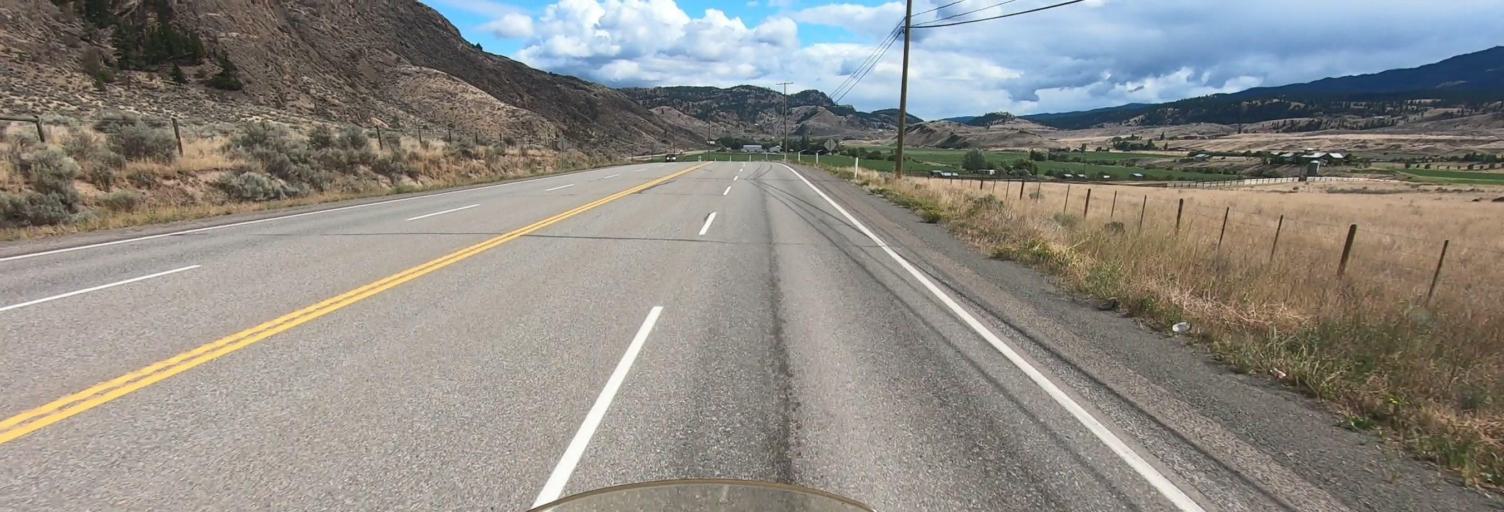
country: CA
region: British Columbia
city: Logan Lake
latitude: 50.7121
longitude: -120.6210
